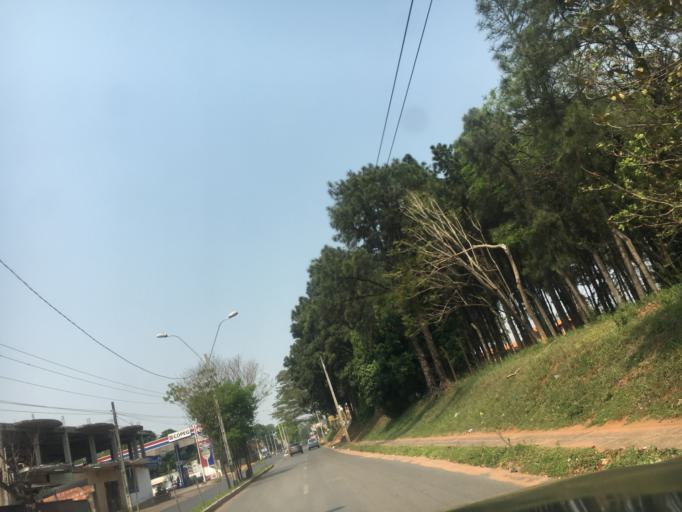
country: PY
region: Central
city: Villa Elisa
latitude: -25.3646
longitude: -57.5902
